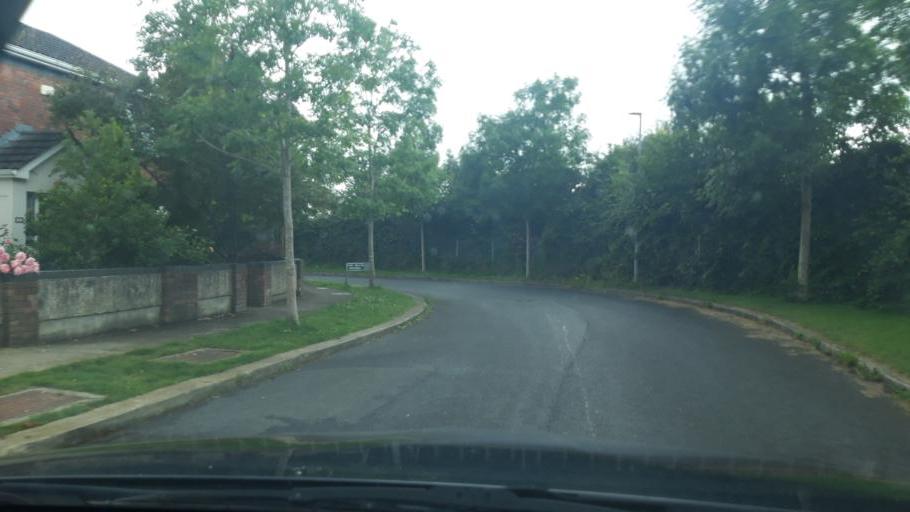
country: IE
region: Leinster
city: Hartstown
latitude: 53.4035
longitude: -6.4394
